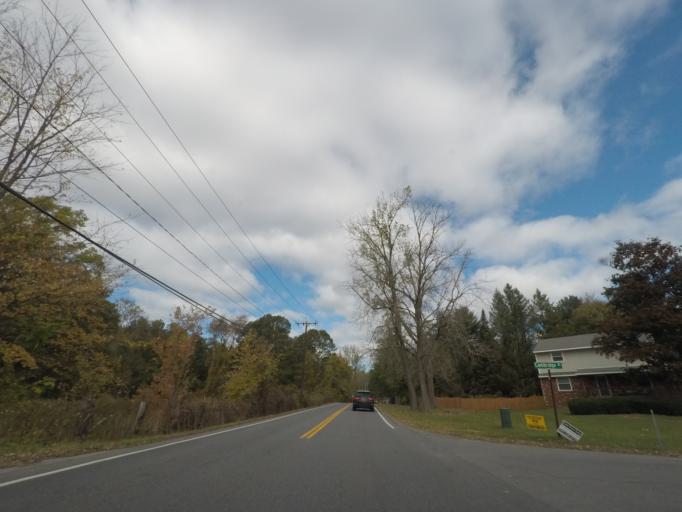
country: US
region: New York
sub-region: Saratoga County
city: Country Knolls
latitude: 42.8420
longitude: -73.7696
